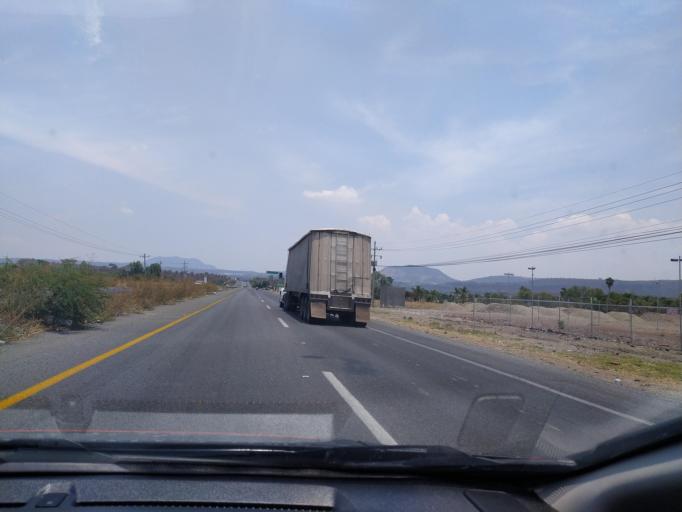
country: MX
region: Jalisco
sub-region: Acatlan de Juarez
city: Villa de los Ninos
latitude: 20.3972
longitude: -103.5937
